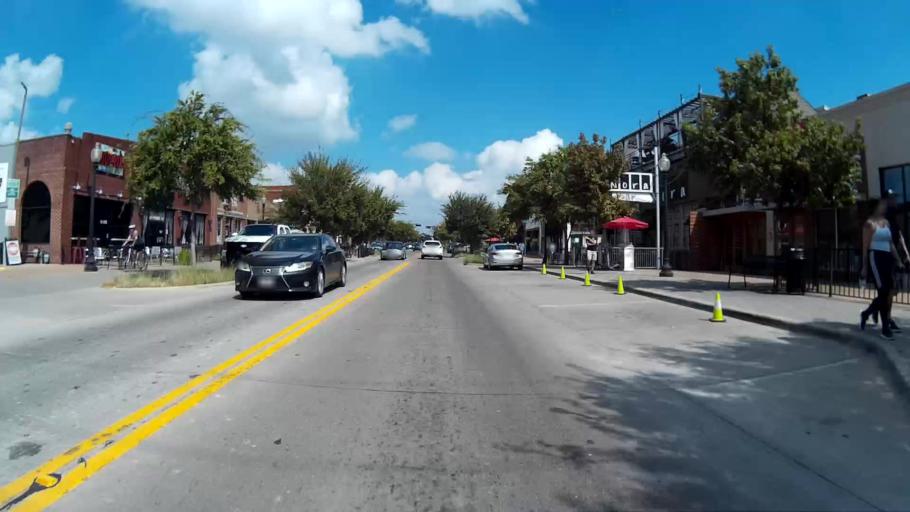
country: US
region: Texas
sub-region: Dallas County
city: Highland Park
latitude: 32.8134
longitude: -96.7702
